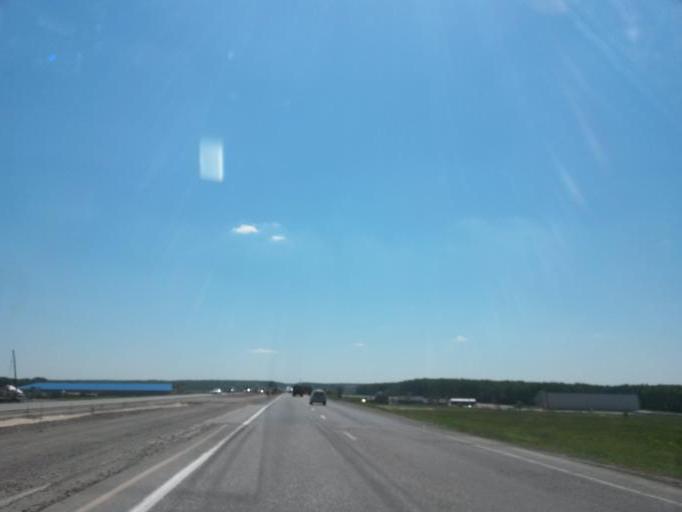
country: RU
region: Moskovskaya
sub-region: Chekhovskiy Rayon
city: Chekhov
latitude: 55.1465
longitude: 37.5541
